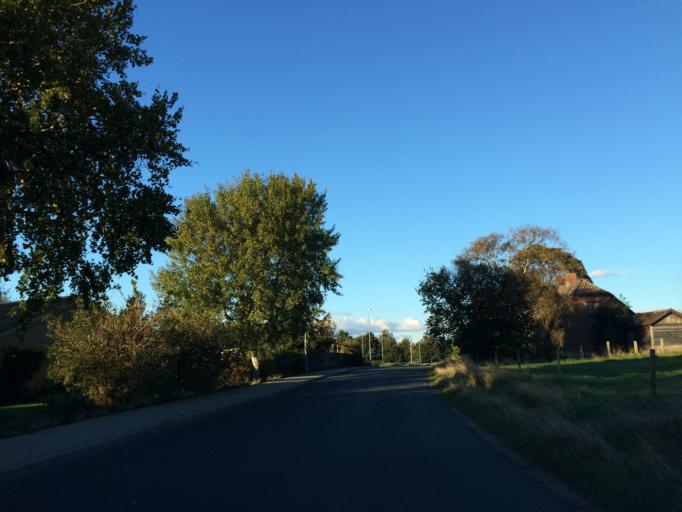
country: DK
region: Central Jutland
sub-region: Silkeborg Kommune
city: Svejbaek
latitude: 56.1887
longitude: 9.6927
